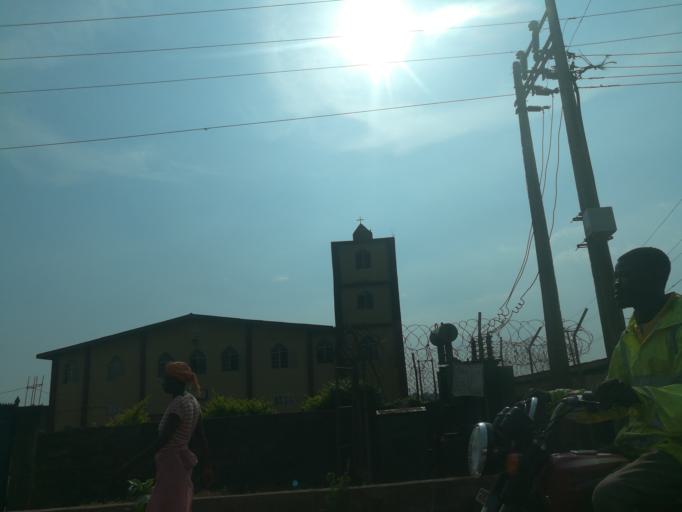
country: NG
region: Lagos
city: Ikorodu
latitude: 6.6683
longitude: 3.6710
